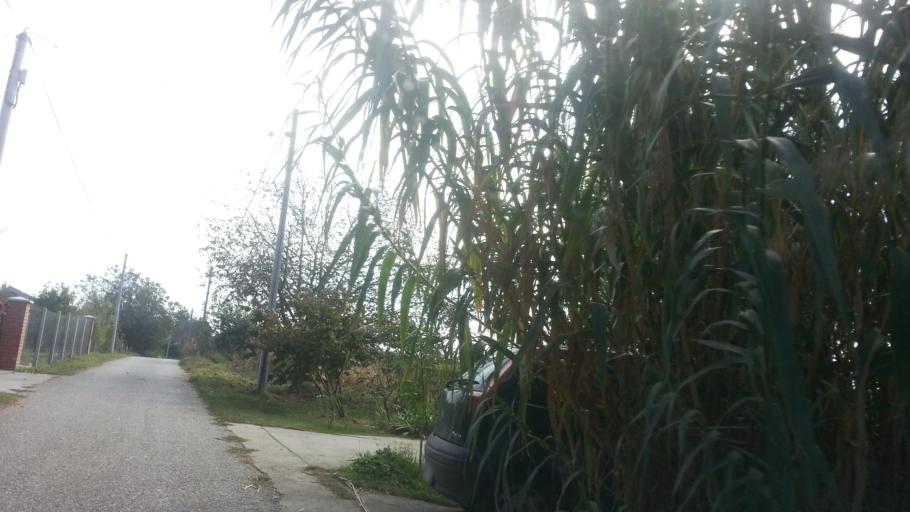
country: RS
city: Surduk
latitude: 45.0758
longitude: 20.3246
